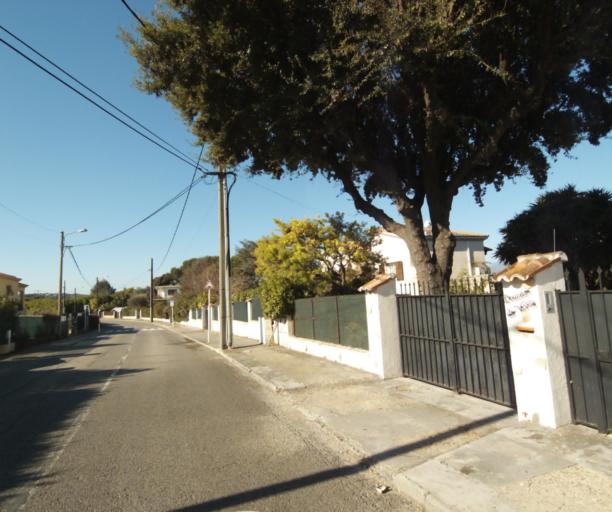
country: FR
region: Provence-Alpes-Cote d'Azur
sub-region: Departement des Alpes-Maritimes
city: Biot
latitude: 43.6085
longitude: 7.0893
